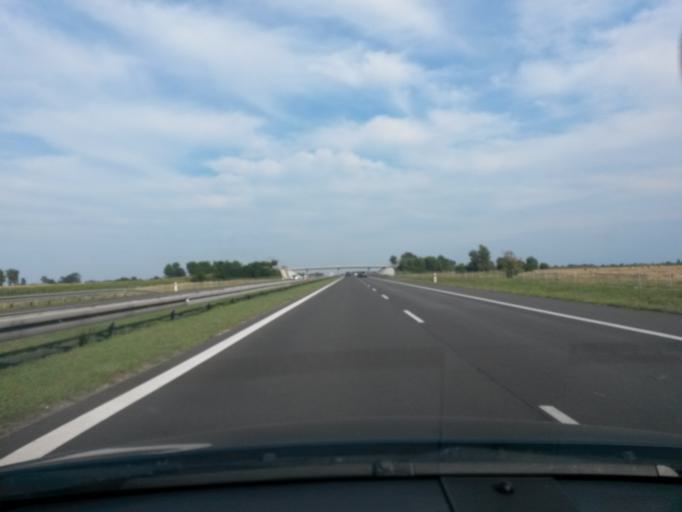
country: PL
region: Greater Poland Voivodeship
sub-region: Powiat slupecki
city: Ladek
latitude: 52.2134
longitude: 17.9823
